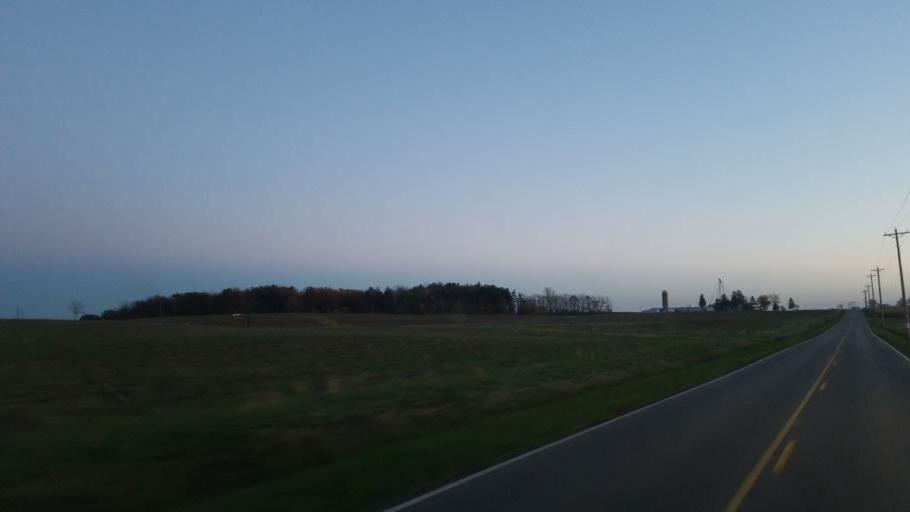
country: US
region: Ohio
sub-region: Richland County
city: Shelby
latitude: 40.9082
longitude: -82.7435
